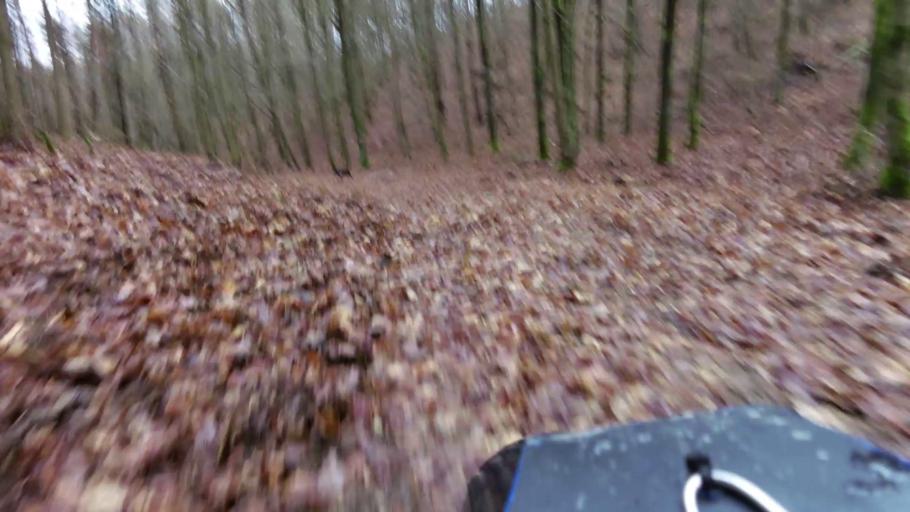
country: PL
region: Lubusz
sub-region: Powiat gorzowski
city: Bogdaniec
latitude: 52.6945
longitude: 15.0619
